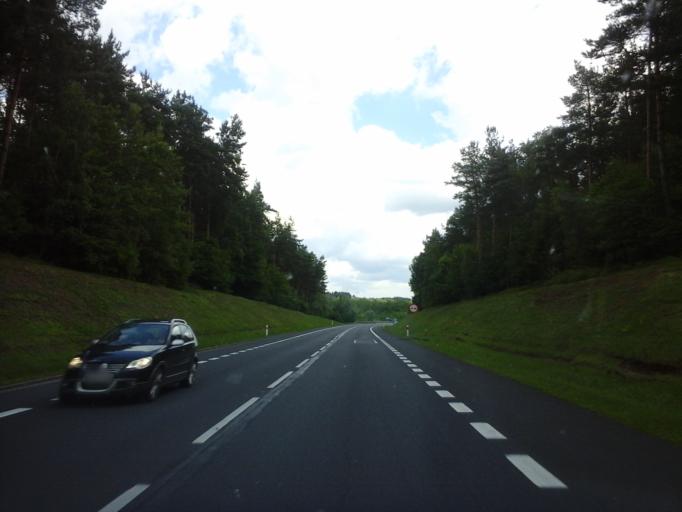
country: PL
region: West Pomeranian Voivodeship
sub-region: Powiat bialogardzki
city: Karlino
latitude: 54.0421
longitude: 15.8983
